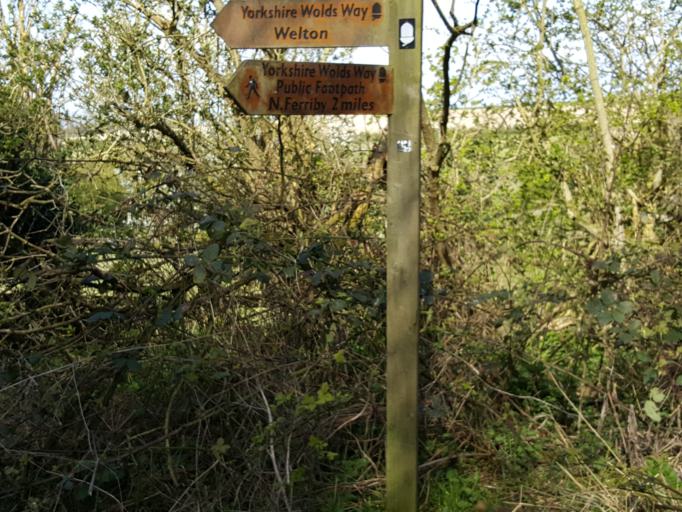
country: GB
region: England
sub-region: East Riding of Yorkshire
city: Welton
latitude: 53.7364
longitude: -0.5398
